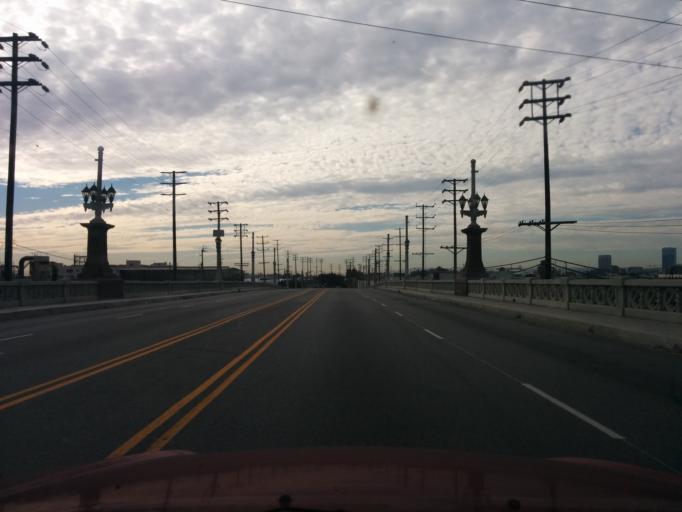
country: US
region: California
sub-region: Los Angeles County
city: Boyle Heights
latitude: 34.0256
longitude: -118.2250
